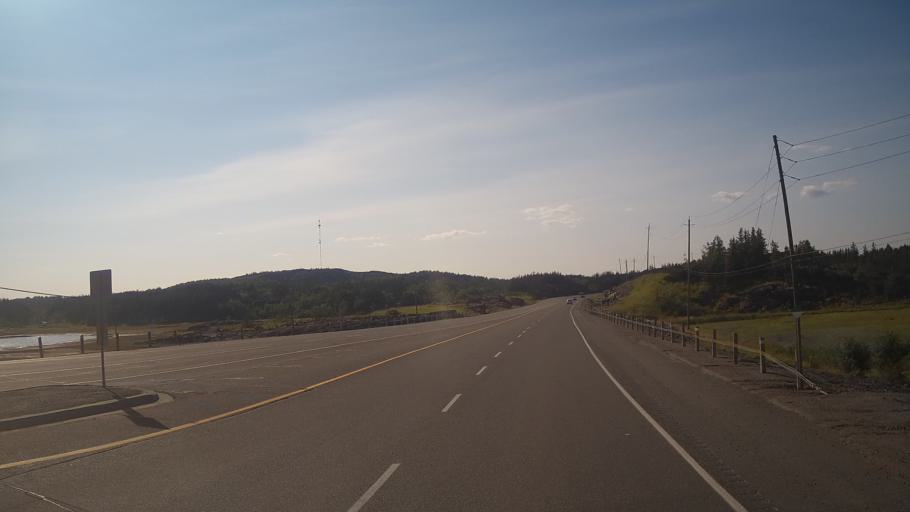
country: CA
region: Ontario
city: Greater Sudbury
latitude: 46.5056
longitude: -81.0469
